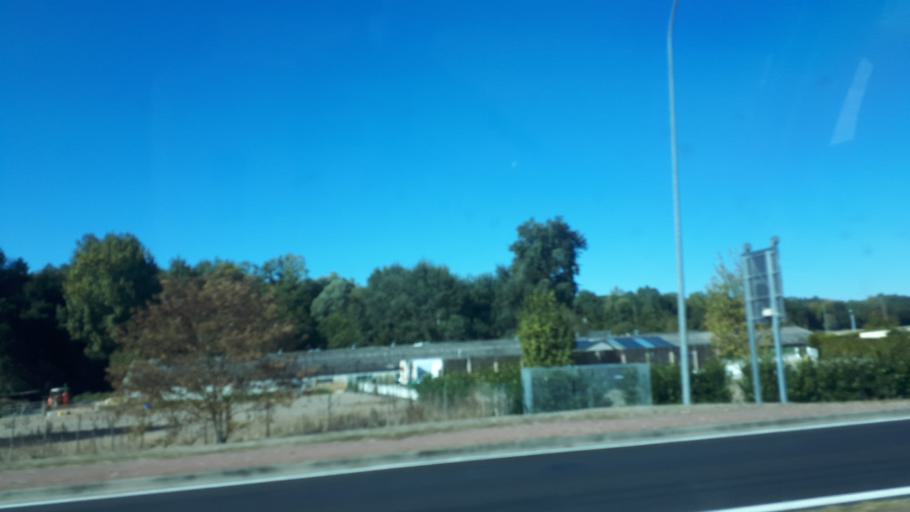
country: FR
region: Centre
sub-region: Departement d'Eure-et-Loir
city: Chateaudun
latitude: 48.0965
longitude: 1.3309
